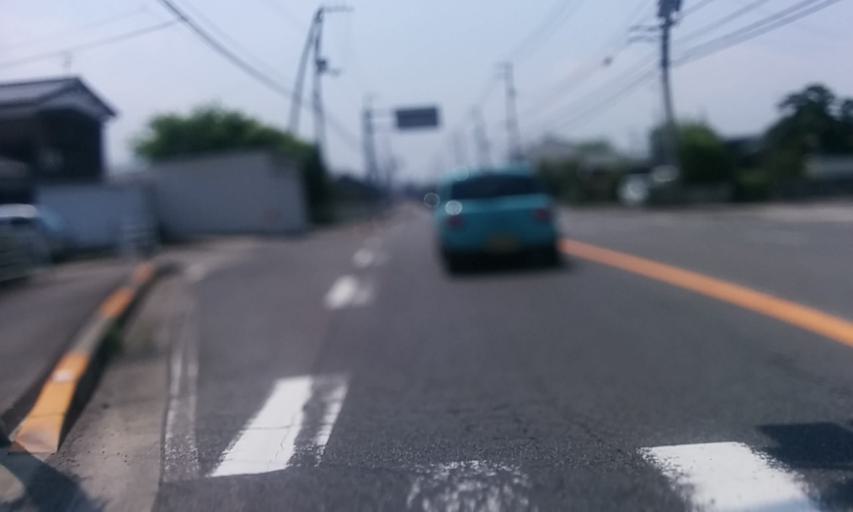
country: JP
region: Ehime
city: Saijo
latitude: 33.9110
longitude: 133.1984
